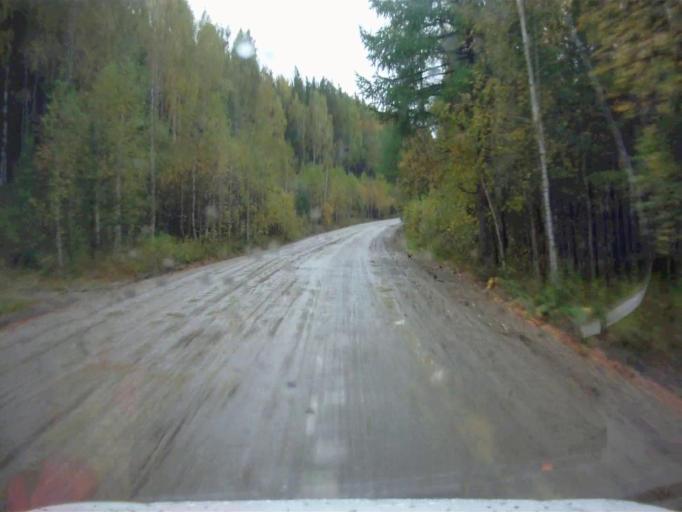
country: RU
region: Chelyabinsk
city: Kyshtym
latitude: 55.7503
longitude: 60.4872
